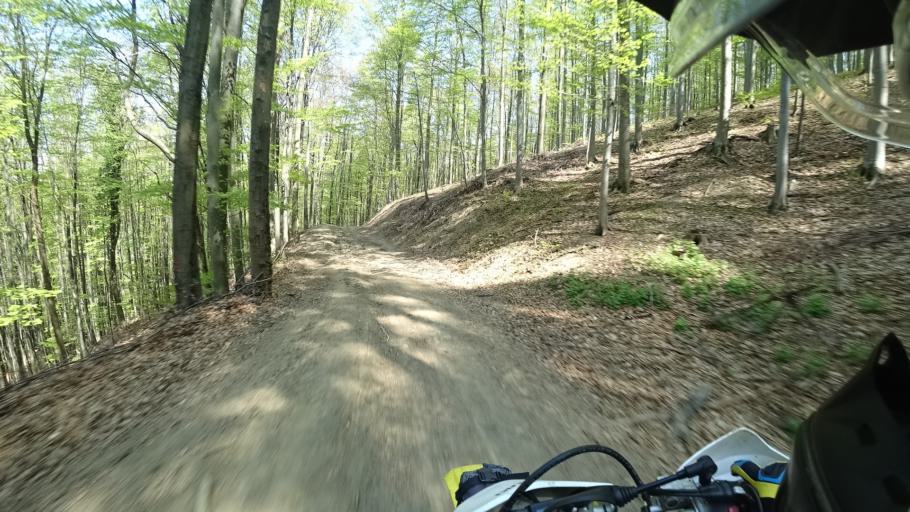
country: HR
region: Zagrebacka
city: Jablanovec
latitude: 45.8991
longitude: 15.9127
